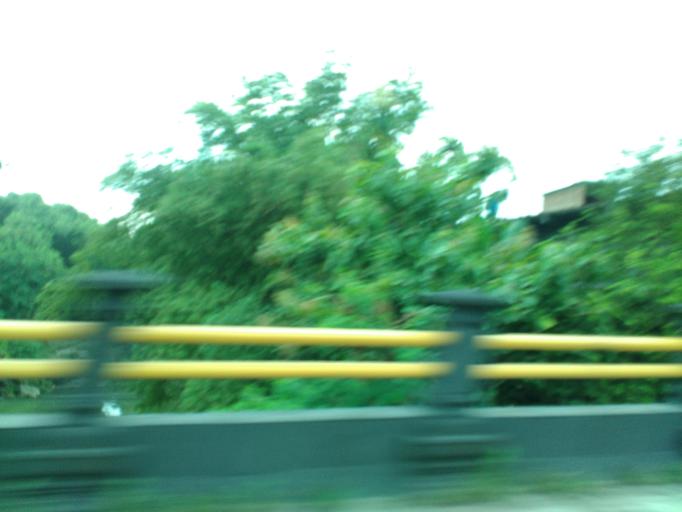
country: ID
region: Central Java
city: Gatak
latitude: -7.5936
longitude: 110.7028
